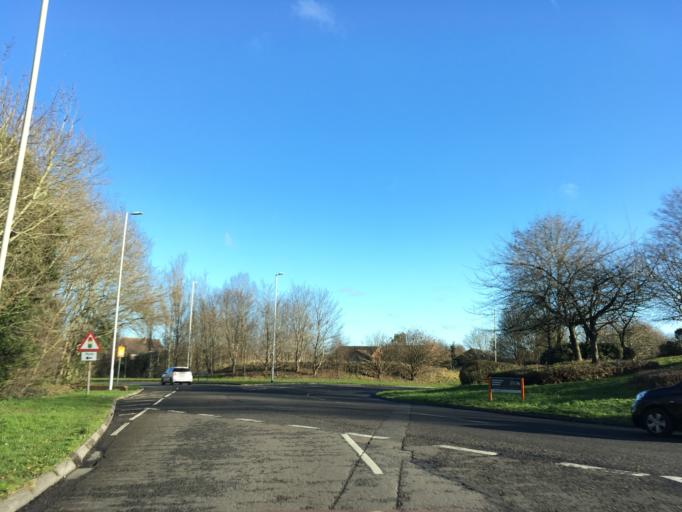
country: GB
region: England
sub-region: Wiltshire
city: Lydiard Tregoze
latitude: 51.5566
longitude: -1.8279
